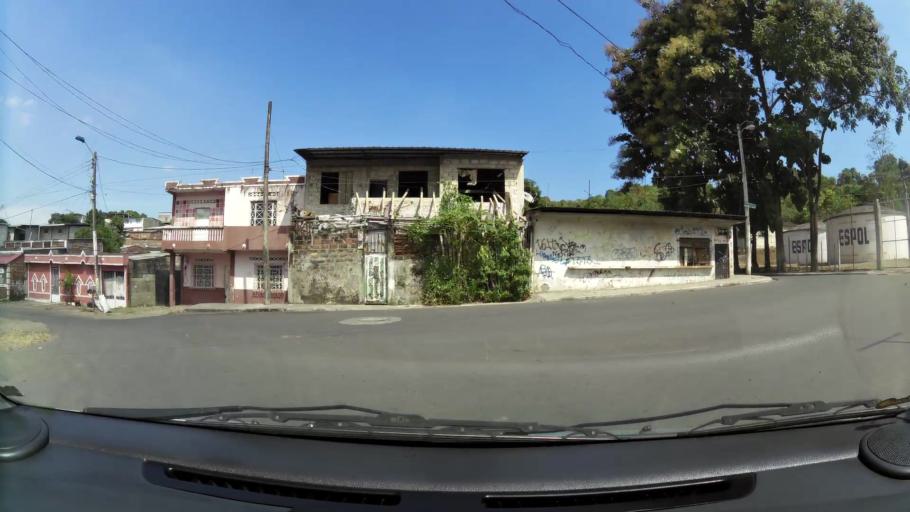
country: EC
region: Guayas
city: Santa Lucia
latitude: -2.1445
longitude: -79.9437
